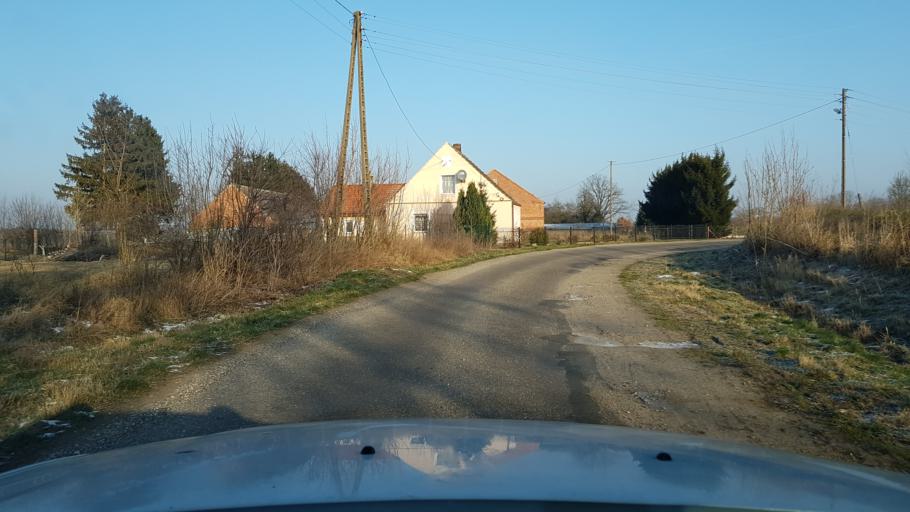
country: PL
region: West Pomeranian Voivodeship
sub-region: Powiat bialogardzki
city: Bialogard
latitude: 54.0714
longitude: 16.0865
